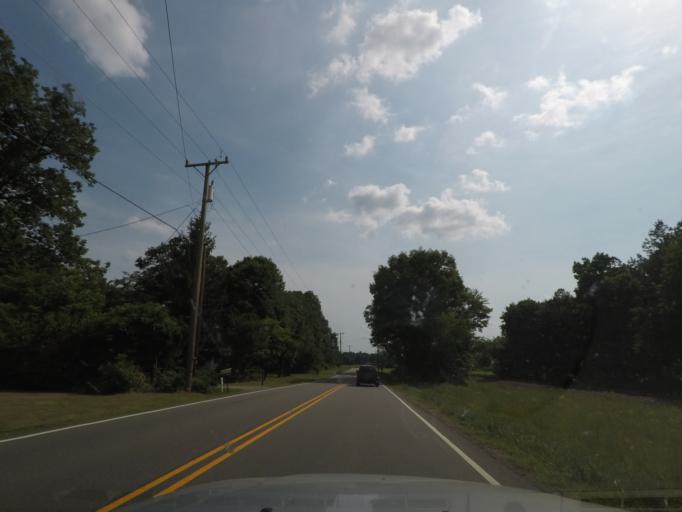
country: US
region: Virginia
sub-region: Buckingham County
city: Buckingham
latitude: 37.5524
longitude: -78.4420
